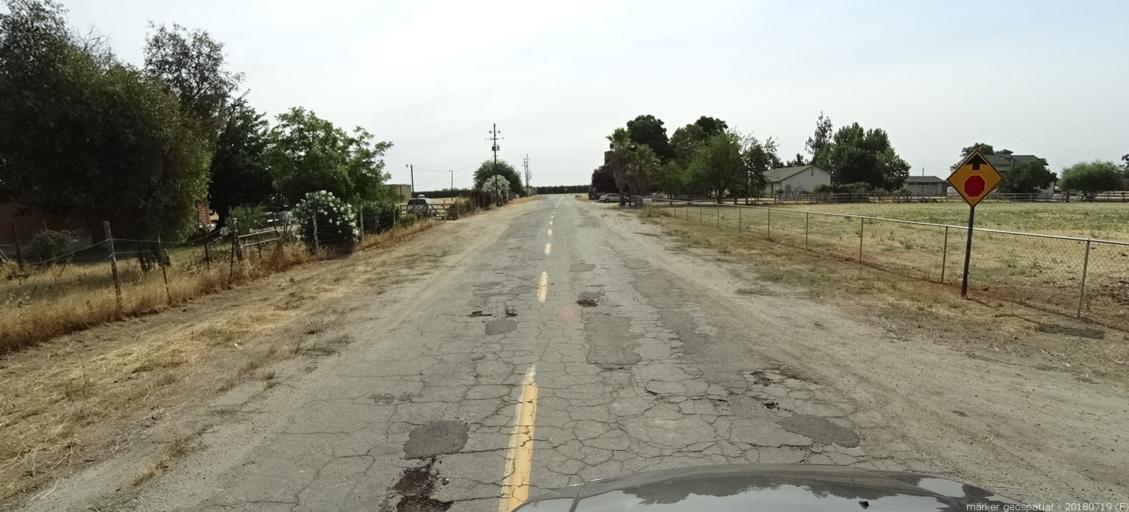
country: US
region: California
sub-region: Madera County
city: Fairmead
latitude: 37.1055
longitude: -120.2042
